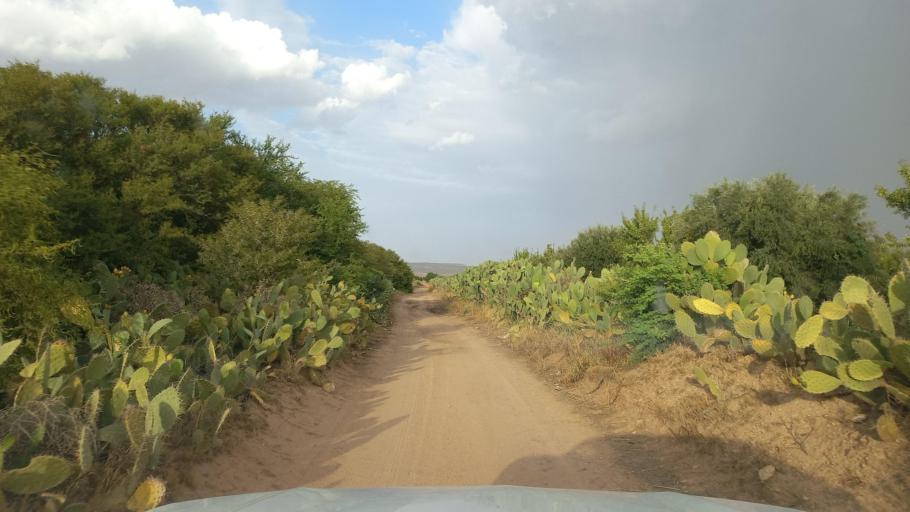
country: TN
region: Al Qasrayn
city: Kasserine
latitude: 35.2824
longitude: 9.0606
